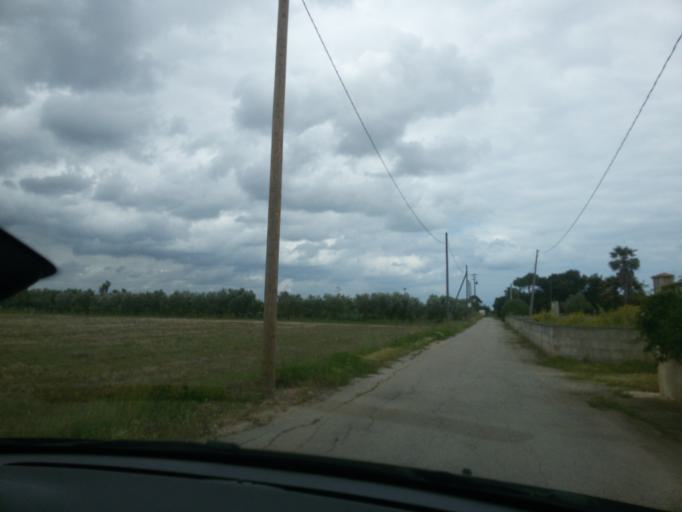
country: IT
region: Apulia
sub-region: Provincia di Brindisi
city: Brindisi
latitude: 40.6349
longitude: 17.8763
